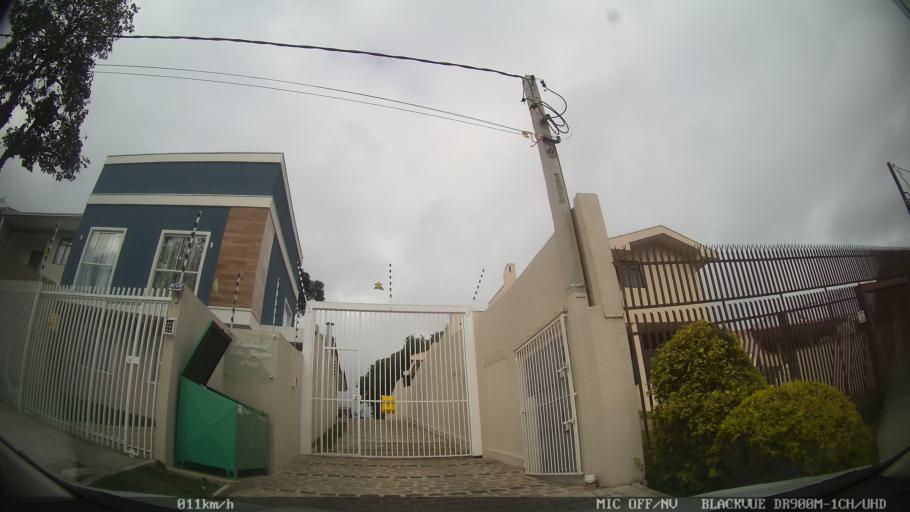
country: BR
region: Parana
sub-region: Almirante Tamandare
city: Almirante Tamandare
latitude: -25.3617
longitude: -49.2650
